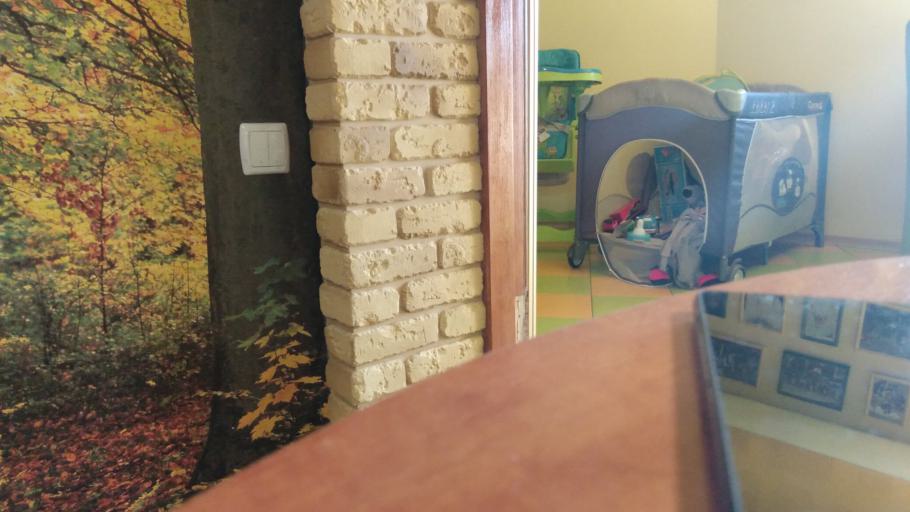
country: RU
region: Tverskaya
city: Bologoye
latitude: 57.9426
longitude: 34.1790
